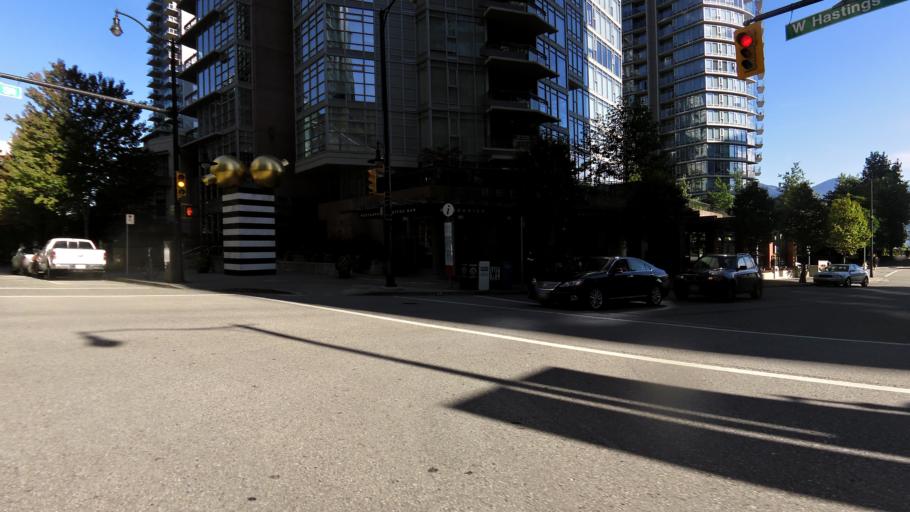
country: CA
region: British Columbia
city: West End
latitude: 49.2875
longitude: -123.1204
